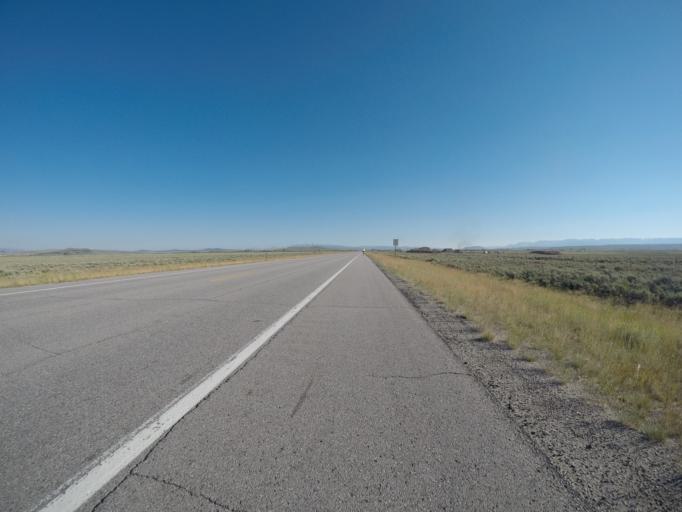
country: US
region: Wyoming
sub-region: Sublette County
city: Pinedale
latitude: 42.9651
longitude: -110.0887
